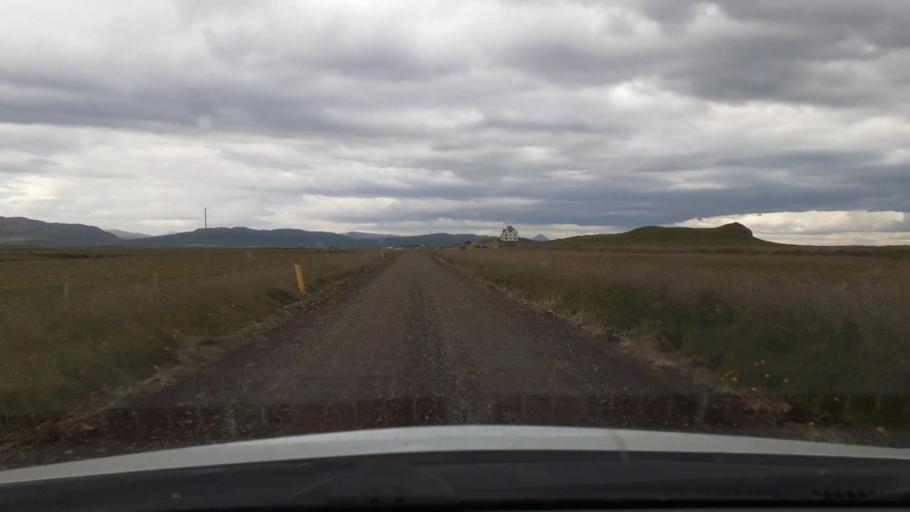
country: IS
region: West
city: Borgarnes
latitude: 64.6497
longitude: -21.8853
